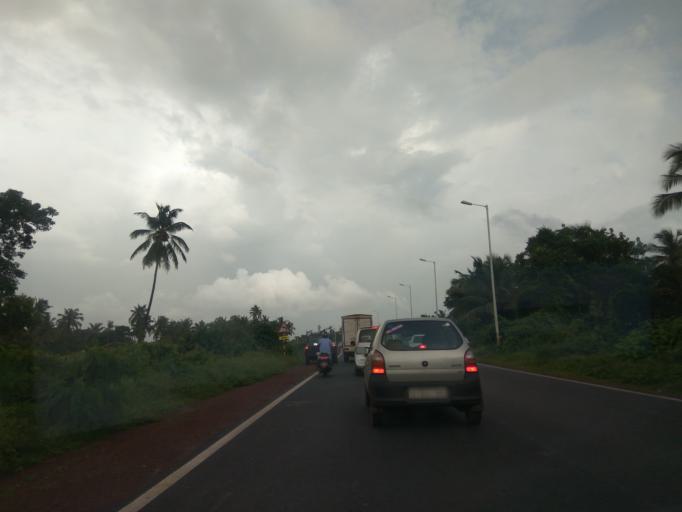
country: IN
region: Goa
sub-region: North Goa
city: Goa Velha
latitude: 15.4254
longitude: 73.8955
